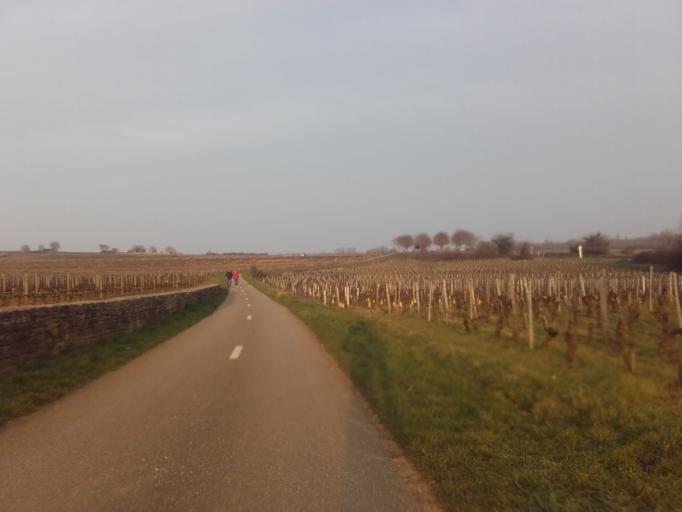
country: FR
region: Bourgogne
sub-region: Departement de Saone-et-Loire
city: Chagny
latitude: 46.9143
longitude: 4.7113
